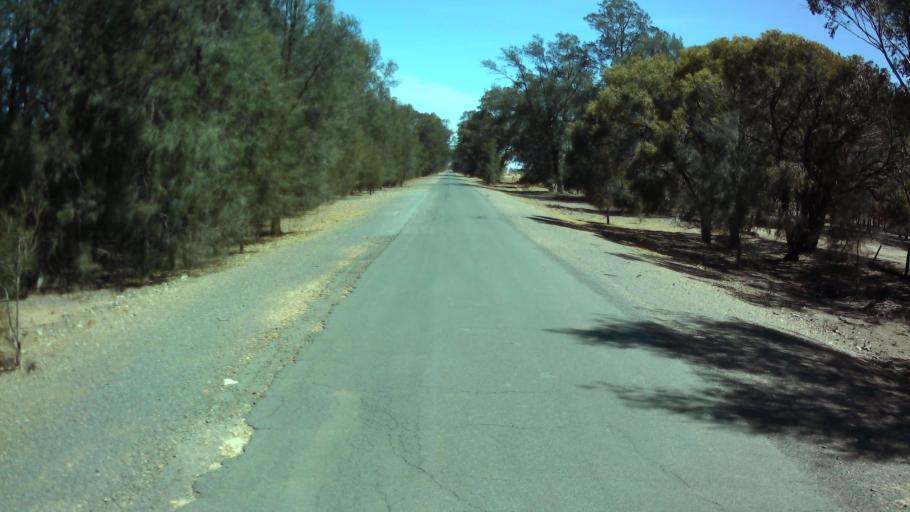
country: AU
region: New South Wales
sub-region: Weddin
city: Grenfell
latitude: -33.8786
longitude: 147.6905
